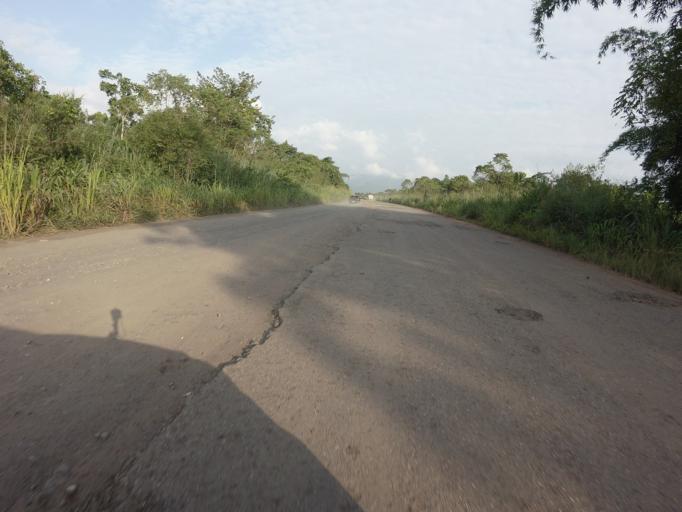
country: GH
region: Volta
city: Kpandu
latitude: 6.9765
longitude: 0.4496
